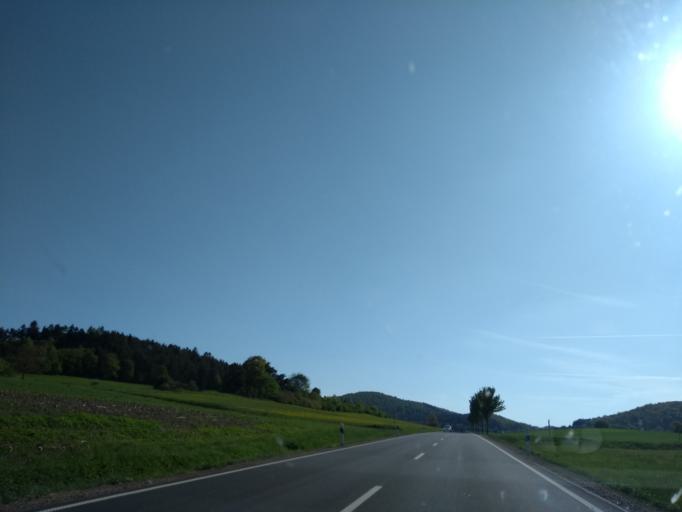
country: DE
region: Hesse
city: Battenberg
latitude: 50.9829
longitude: 8.6172
